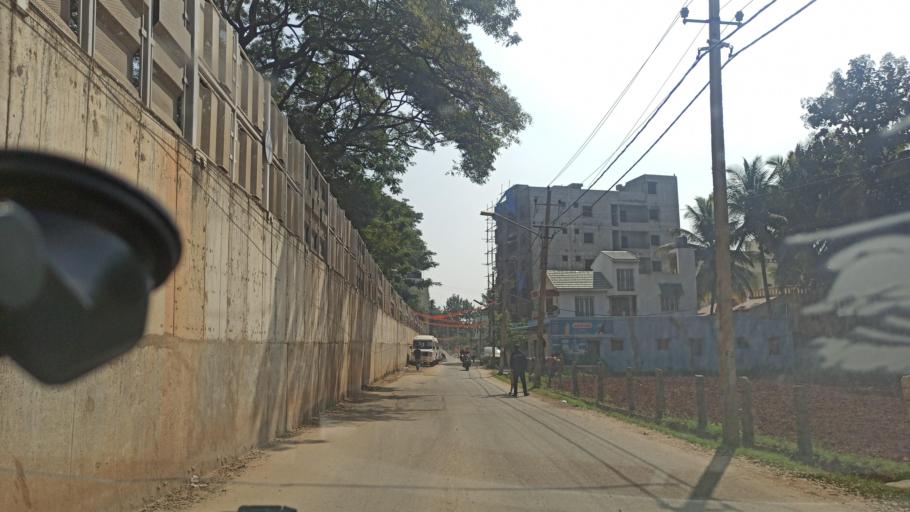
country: IN
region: Karnataka
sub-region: Bangalore Urban
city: Yelahanka
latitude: 13.0673
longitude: 77.5900
